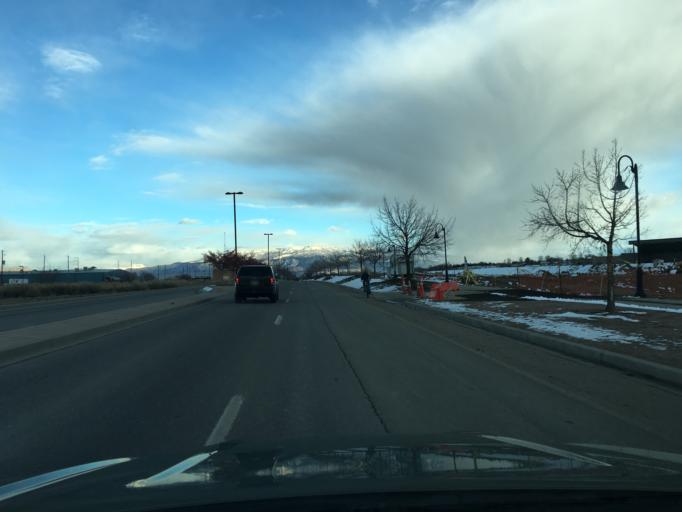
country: US
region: Colorado
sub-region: Mesa County
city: Grand Junction
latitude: 39.0559
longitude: -108.5574
